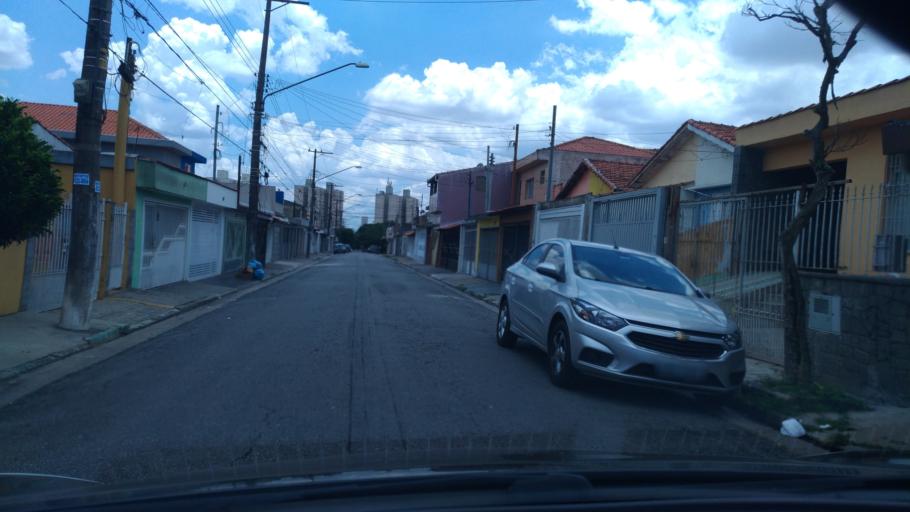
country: BR
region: Sao Paulo
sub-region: Sao Bernardo Do Campo
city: Sao Bernardo do Campo
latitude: -23.7032
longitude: -46.5806
